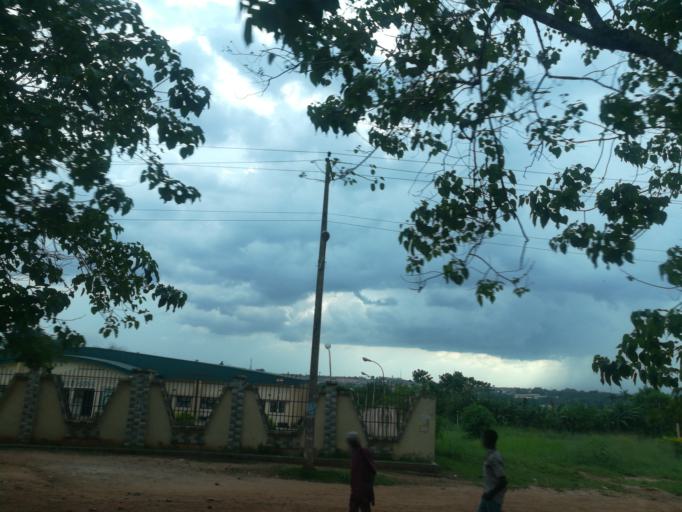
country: NG
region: Oyo
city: Ibadan
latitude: 7.4330
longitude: 3.8898
